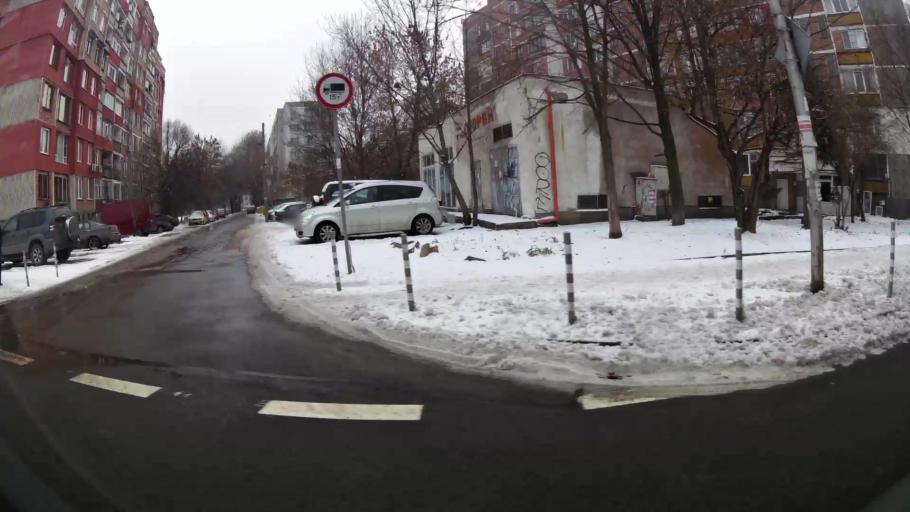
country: BG
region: Sofia-Capital
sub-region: Stolichna Obshtina
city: Sofia
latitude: 42.7092
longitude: 23.3448
